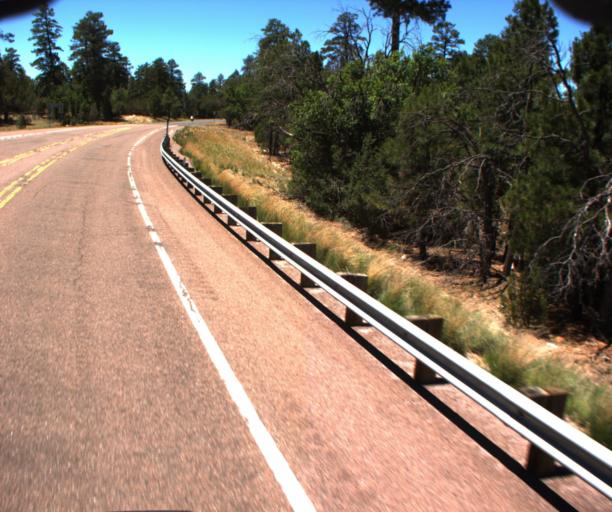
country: US
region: Arizona
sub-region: Gila County
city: Star Valley
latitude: 34.6329
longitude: -111.1111
